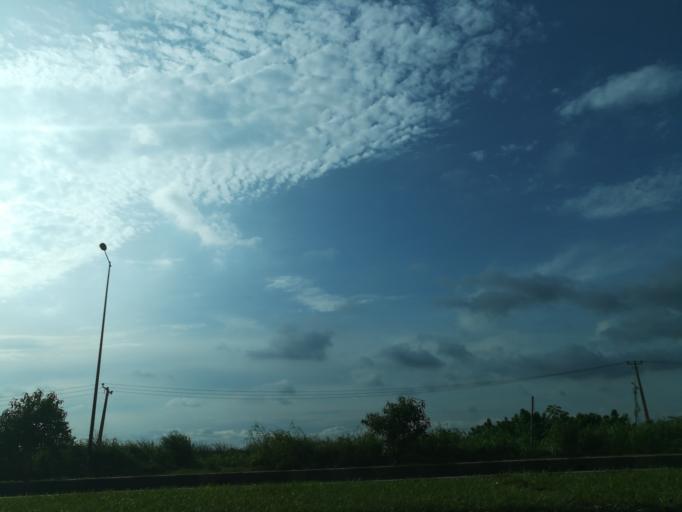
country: NG
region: Lagos
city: Ebute Ikorodu
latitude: 6.6198
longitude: 3.4499
